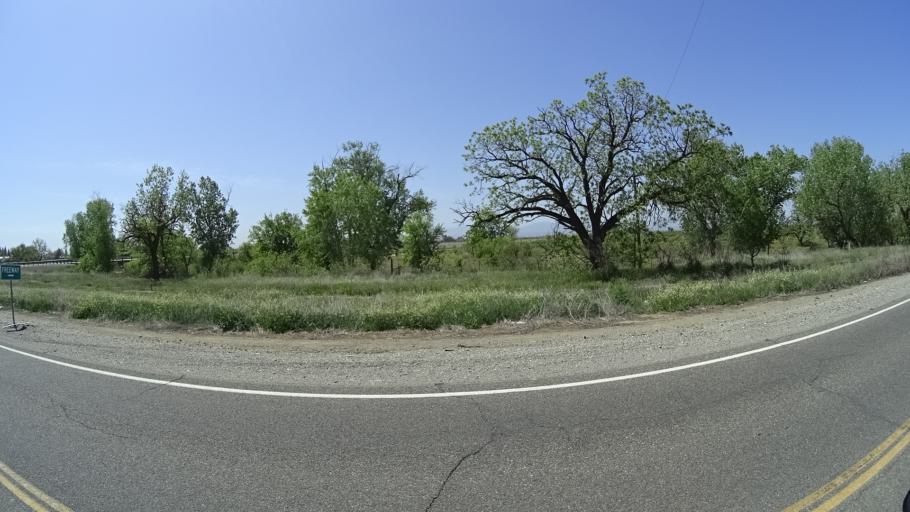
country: US
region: California
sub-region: Glenn County
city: Willows
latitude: 39.6252
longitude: -122.1962
